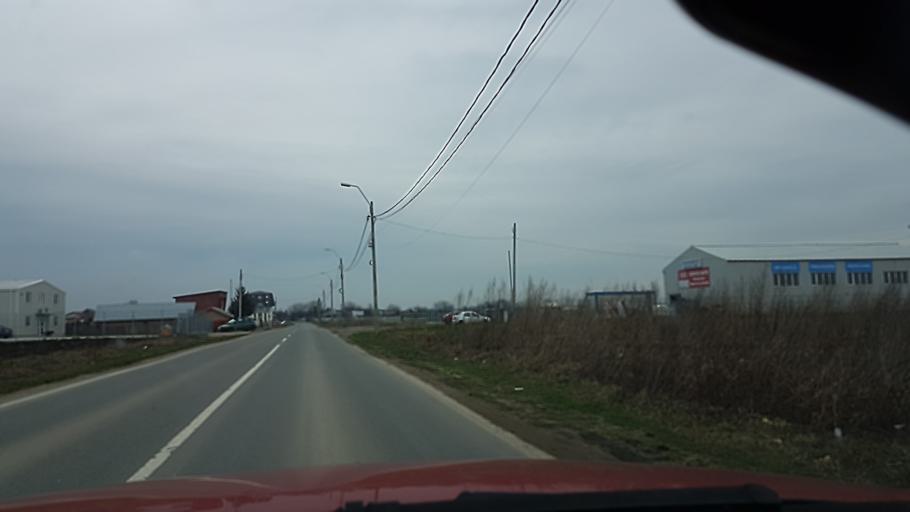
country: RO
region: Ilfov
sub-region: Comuna Balotesti
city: Balotesti
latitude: 44.5976
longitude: 26.1334
